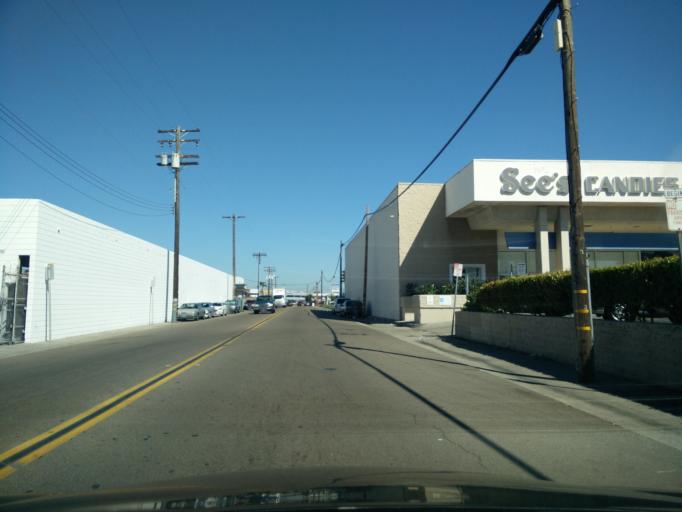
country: US
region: California
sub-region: San Diego County
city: San Diego
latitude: 32.7519
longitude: -117.2034
